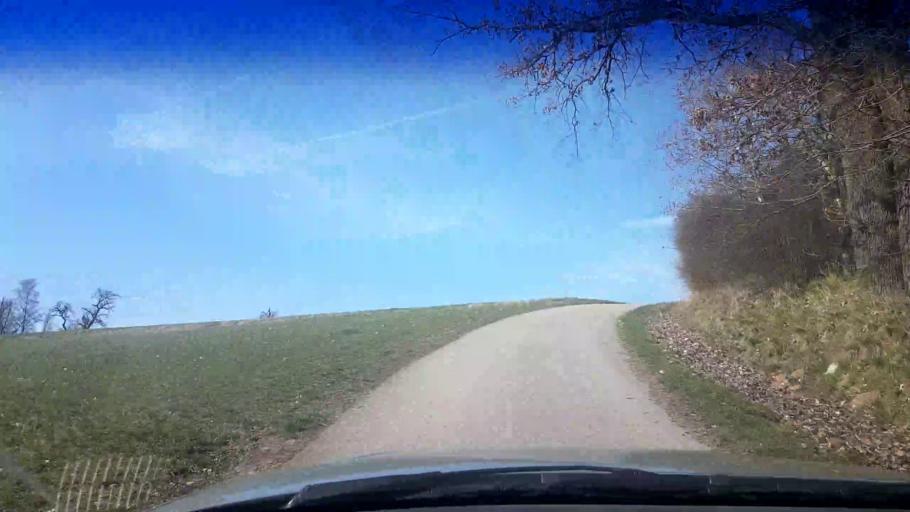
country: DE
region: Bavaria
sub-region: Upper Franconia
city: Bischberg
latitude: 49.8991
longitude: 10.8256
